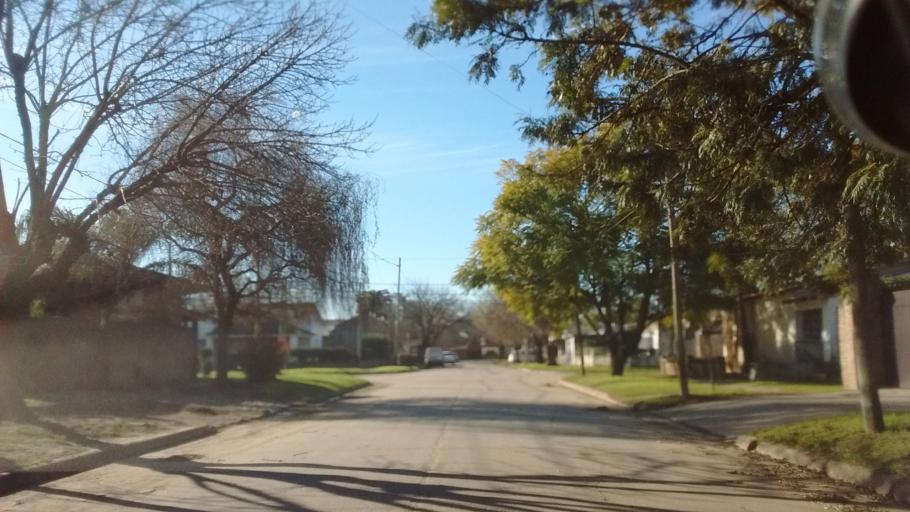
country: AR
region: Santa Fe
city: Funes
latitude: -32.9131
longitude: -60.8153
